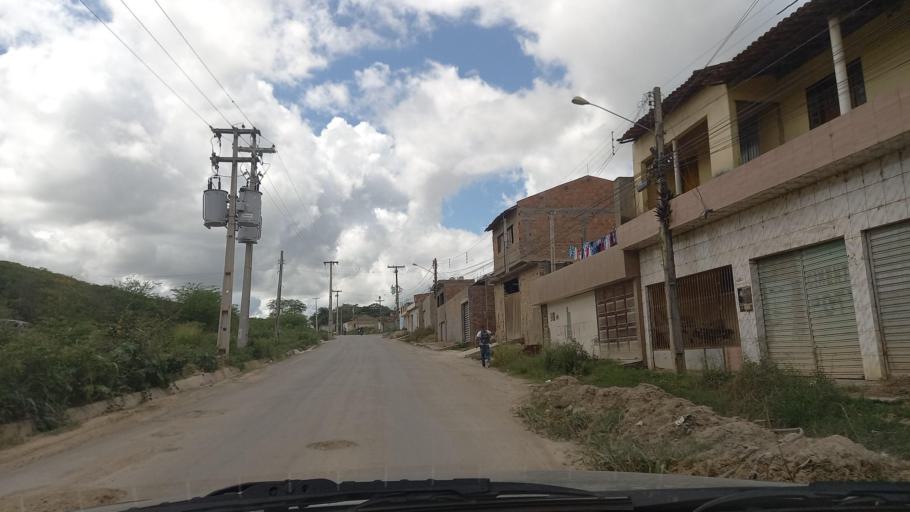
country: BR
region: Pernambuco
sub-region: Caruaru
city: Caruaru
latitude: -8.2760
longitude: -35.9400
